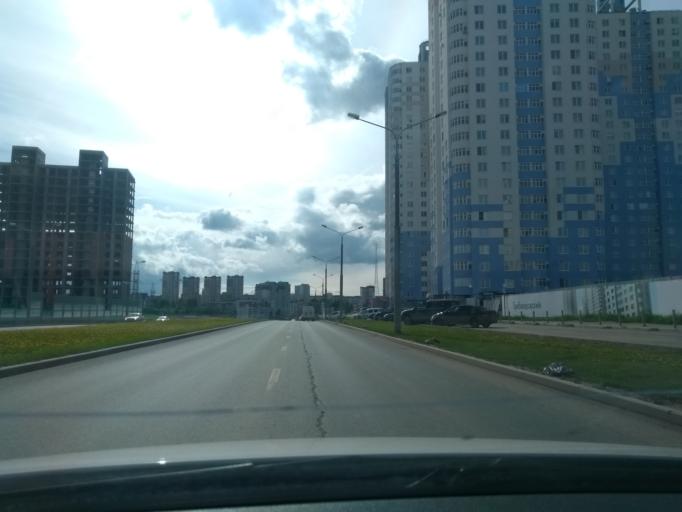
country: RU
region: Perm
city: Perm
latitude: 58.0053
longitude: 56.3233
